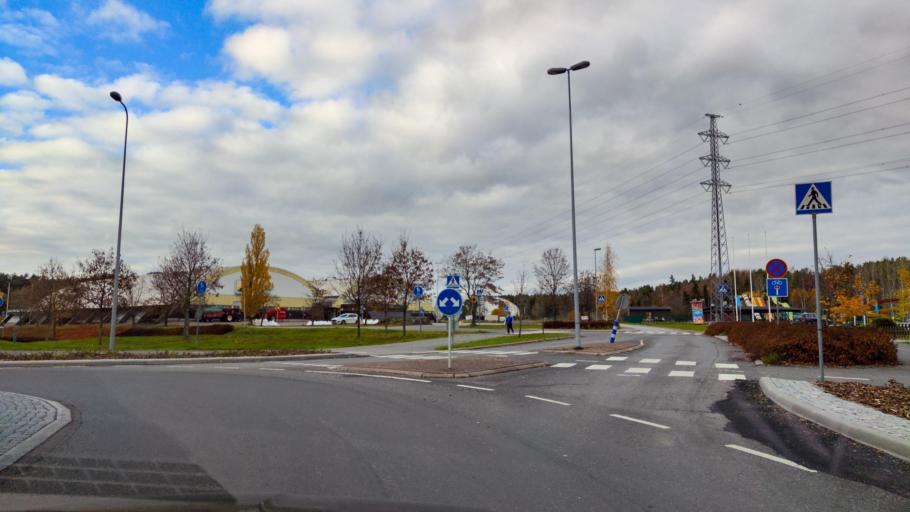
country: FI
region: Varsinais-Suomi
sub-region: Turku
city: Turku
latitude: 60.4769
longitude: 22.2565
